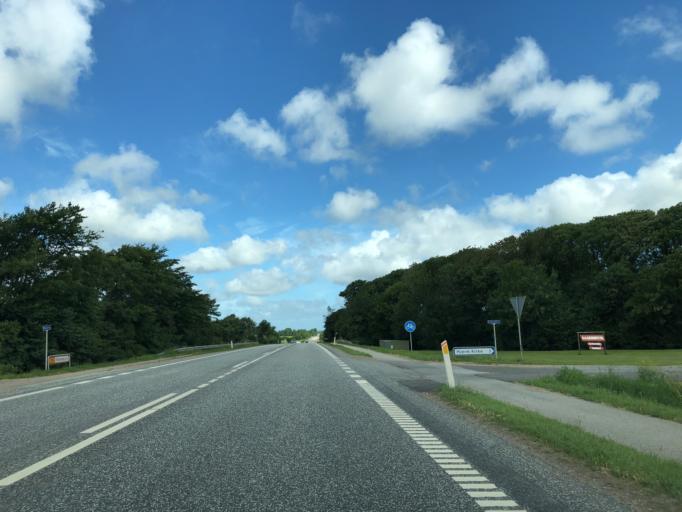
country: DK
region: Central Jutland
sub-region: Struer Kommune
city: Struer
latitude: 56.4272
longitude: 8.5991
